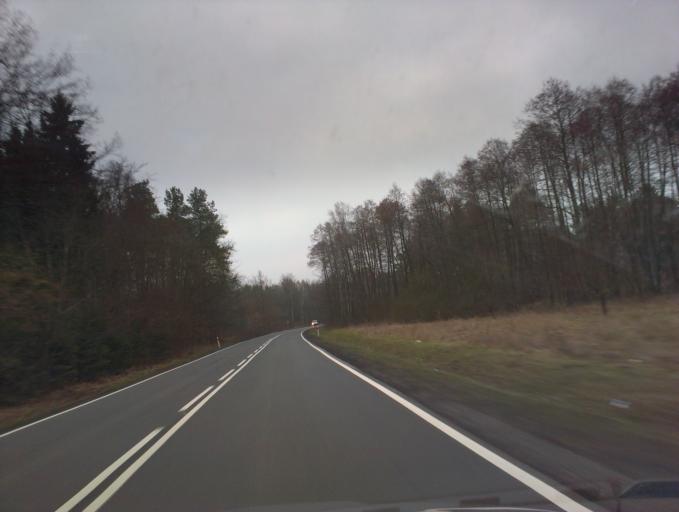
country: PL
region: Greater Poland Voivodeship
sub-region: Powiat pilski
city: Pila
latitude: 53.2296
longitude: 16.7897
